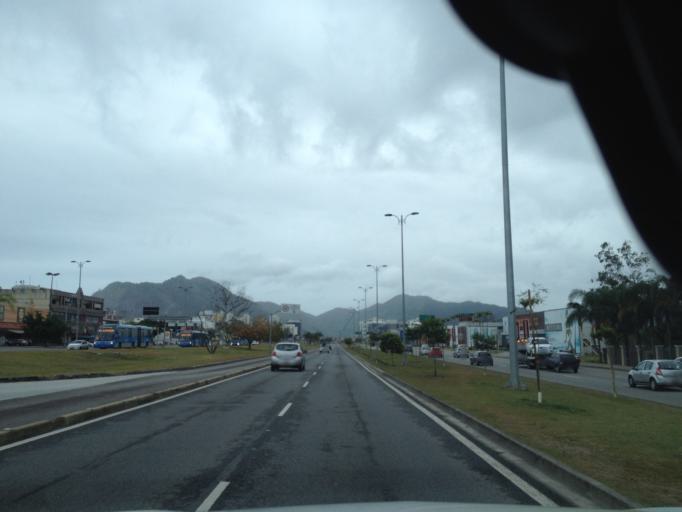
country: BR
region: Rio de Janeiro
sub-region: Nilopolis
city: Nilopolis
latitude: -23.0155
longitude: -43.4717
